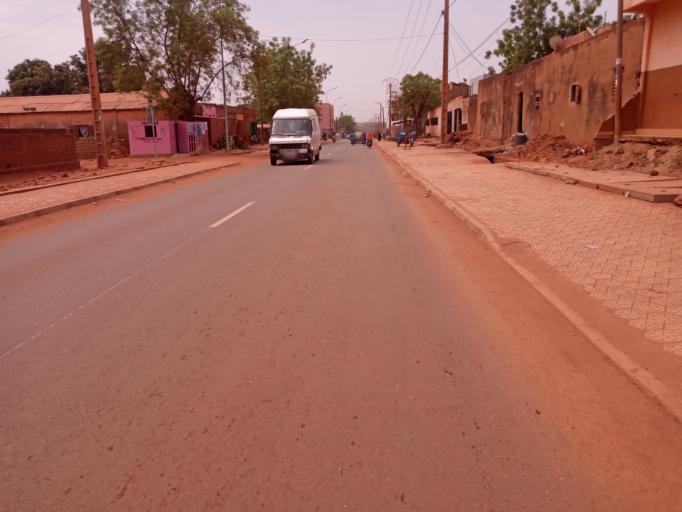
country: ML
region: Bamako
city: Bamako
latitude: 12.5876
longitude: -7.9882
